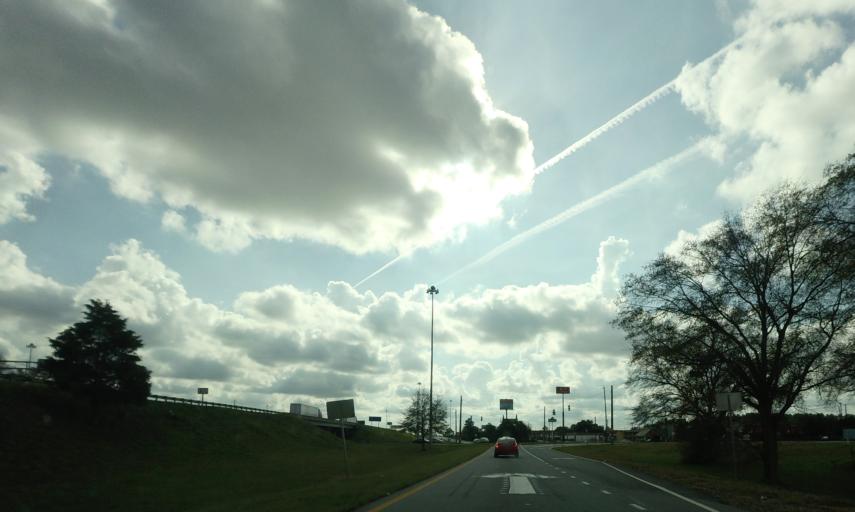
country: US
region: Georgia
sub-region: Houston County
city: Perry
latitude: 32.4730
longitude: -83.7440
